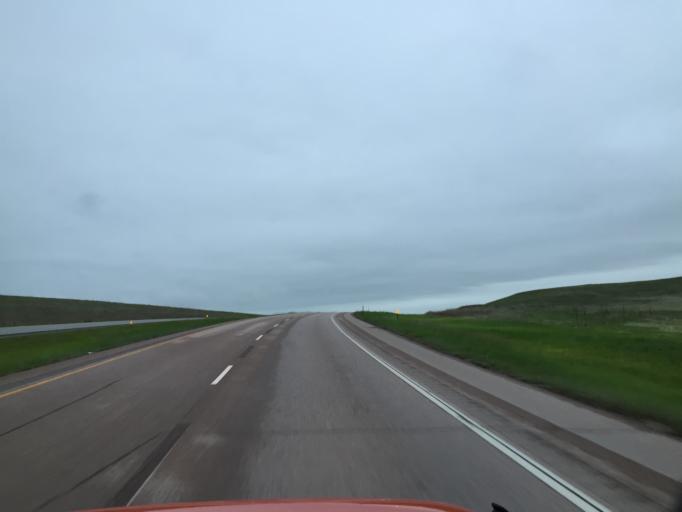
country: US
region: South Dakota
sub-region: Pennington County
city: Colonial Pine Hills
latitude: 43.6973
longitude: -103.2542
